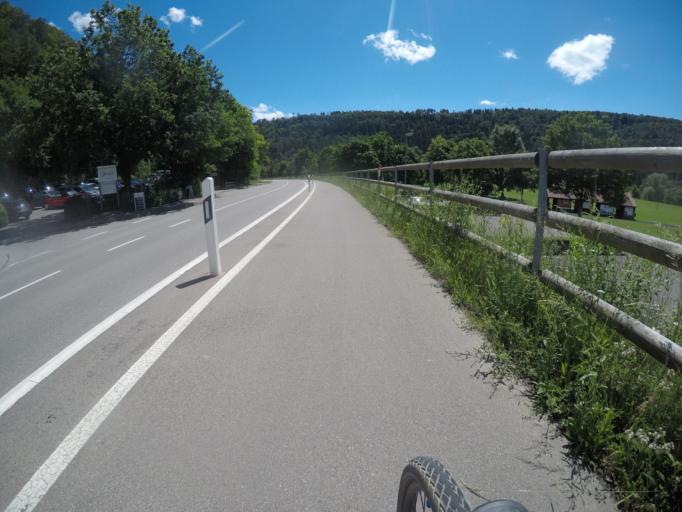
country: DE
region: Baden-Wuerttemberg
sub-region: Tuebingen Region
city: Hirrlingen
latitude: 48.4432
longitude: 8.8375
